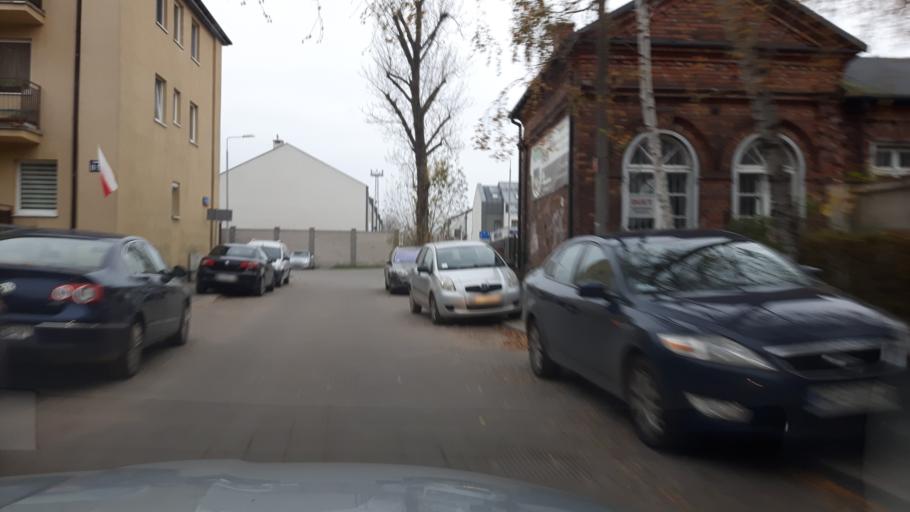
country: PL
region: Masovian Voivodeship
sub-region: Warszawa
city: Targowek
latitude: 52.2819
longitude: 21.0227
